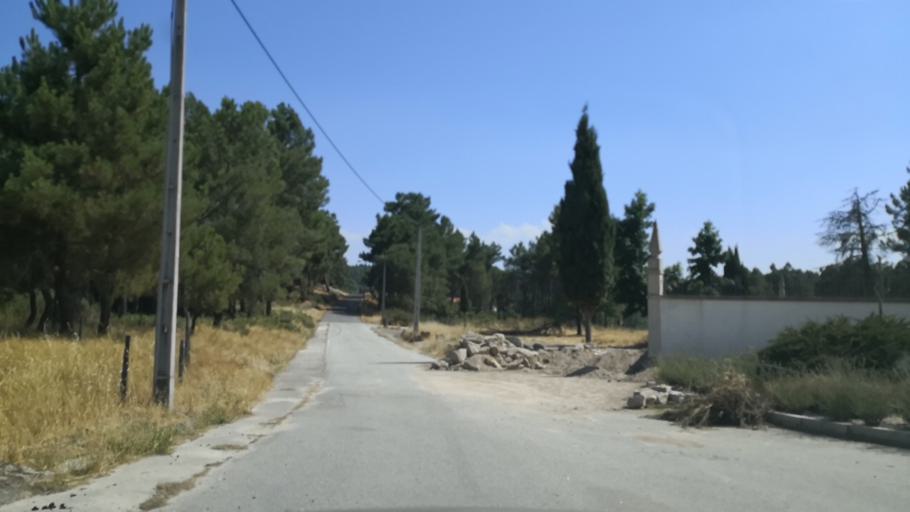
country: PT
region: Vila Real
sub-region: Murca
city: Murca
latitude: 41.3514
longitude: -7.4860
